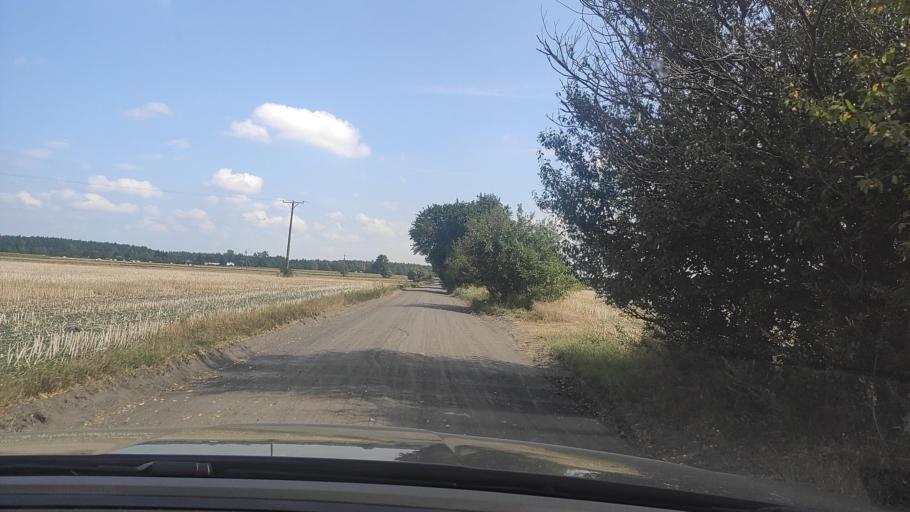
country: PL
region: Greater Poland Voivodeship
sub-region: Powiat poznanski
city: Pobiedziska
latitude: 52.4864
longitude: 17.1947
